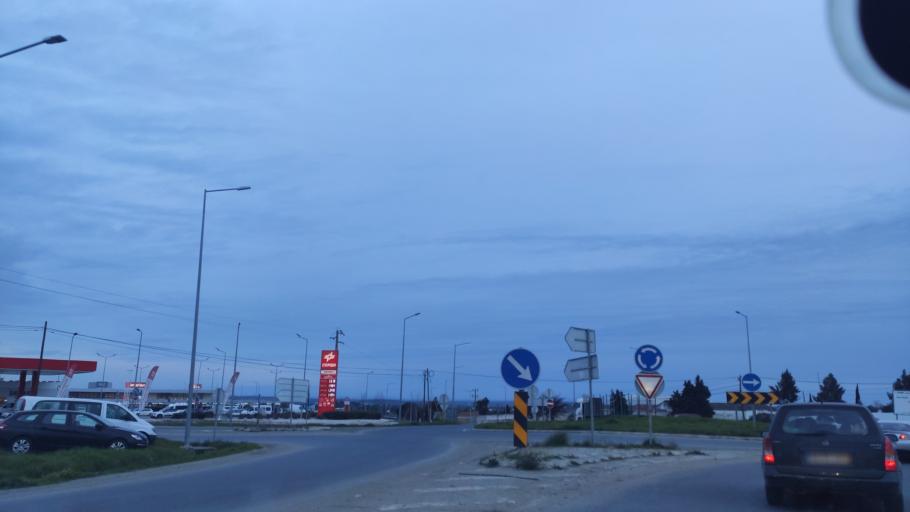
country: PT
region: Beja
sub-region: Beja
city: Beja
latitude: 38.0205
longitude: -7.8482
